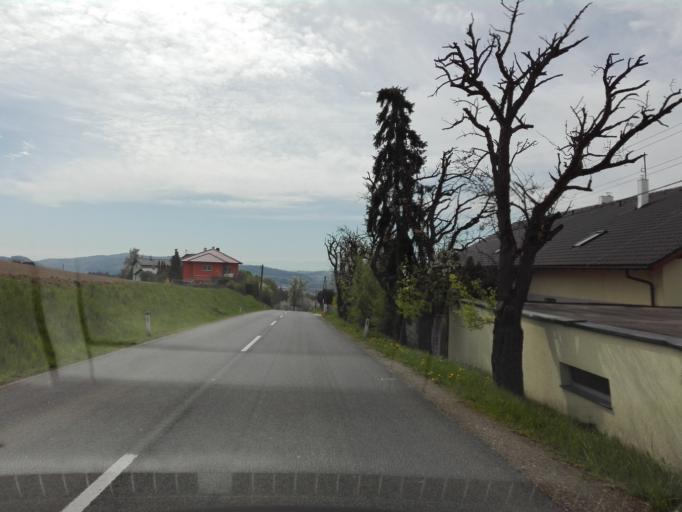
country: AT
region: Upper Austria
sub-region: Politischer Bezirk Urfahr-Umgebung
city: Walding
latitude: 48.3636
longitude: 14.1593
